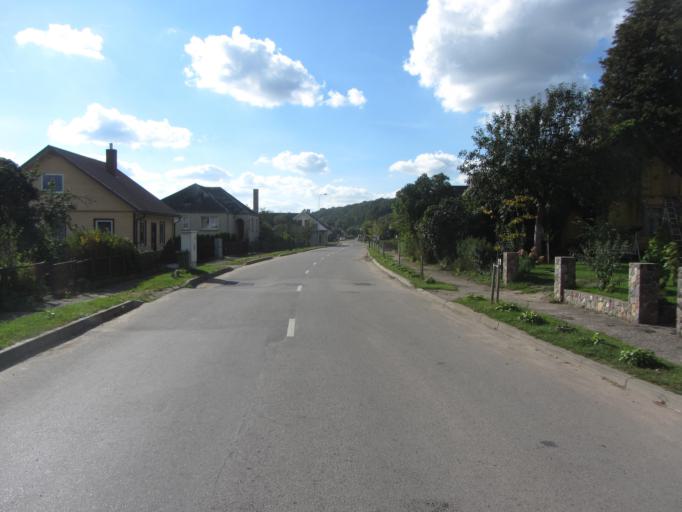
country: LT
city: Vilkija
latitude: 55.0791
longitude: 23.4093
